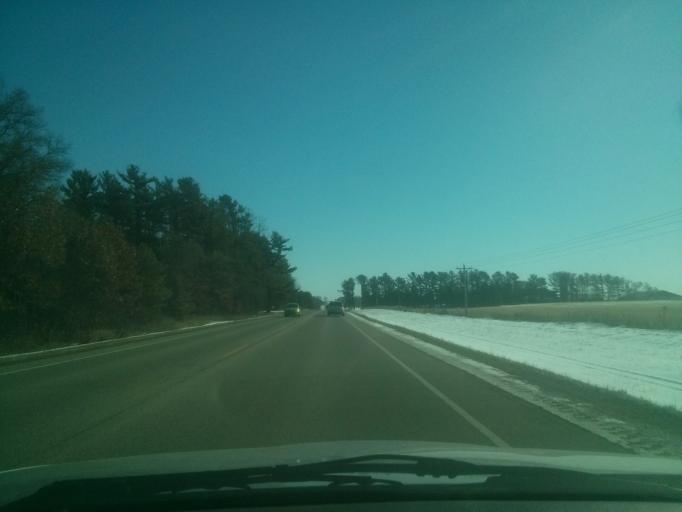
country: US
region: Wisconsin
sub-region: Saint Croix County
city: New Richmond
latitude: 45.1366
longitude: -92.4021
